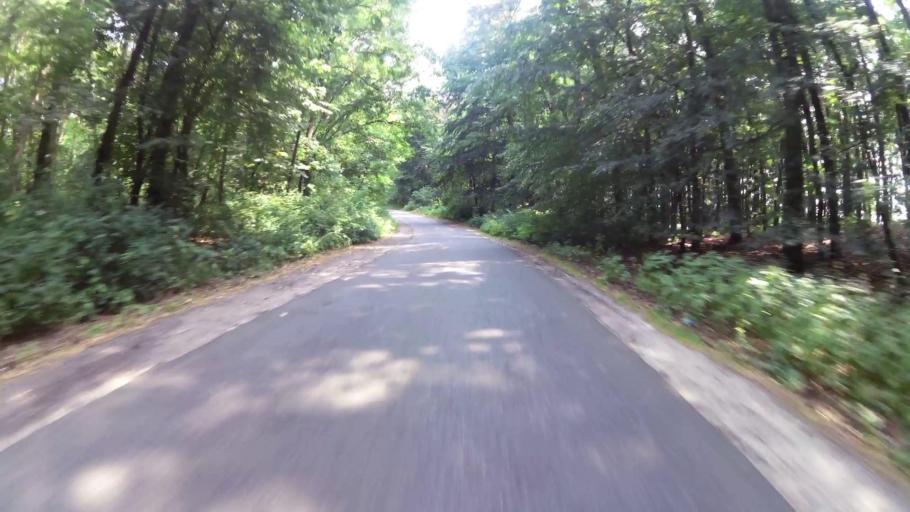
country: PL
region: West Pomeranian Voivodeship
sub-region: Powiat gryfinski
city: Chojna
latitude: 52.9093
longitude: 14.4762
